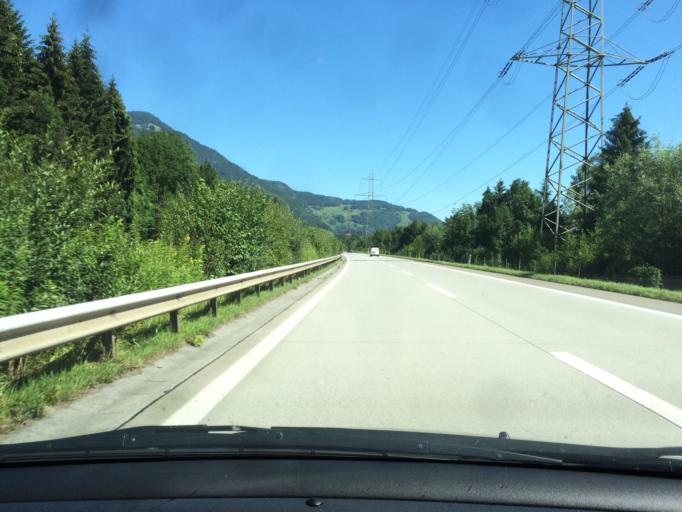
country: LI
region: Ruggell
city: Ruggell
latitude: 47.2636
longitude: 9.5283
